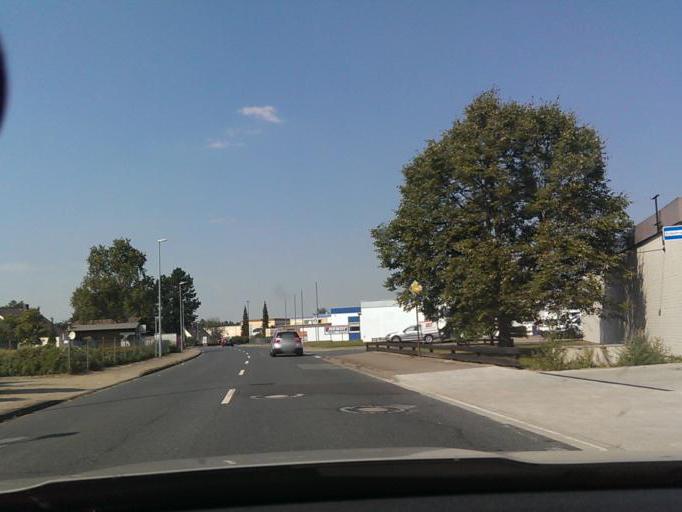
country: DE
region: Lower Saxony
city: Isernhagen Farster Bauerschaft
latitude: 52.4928
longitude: 9.8401
